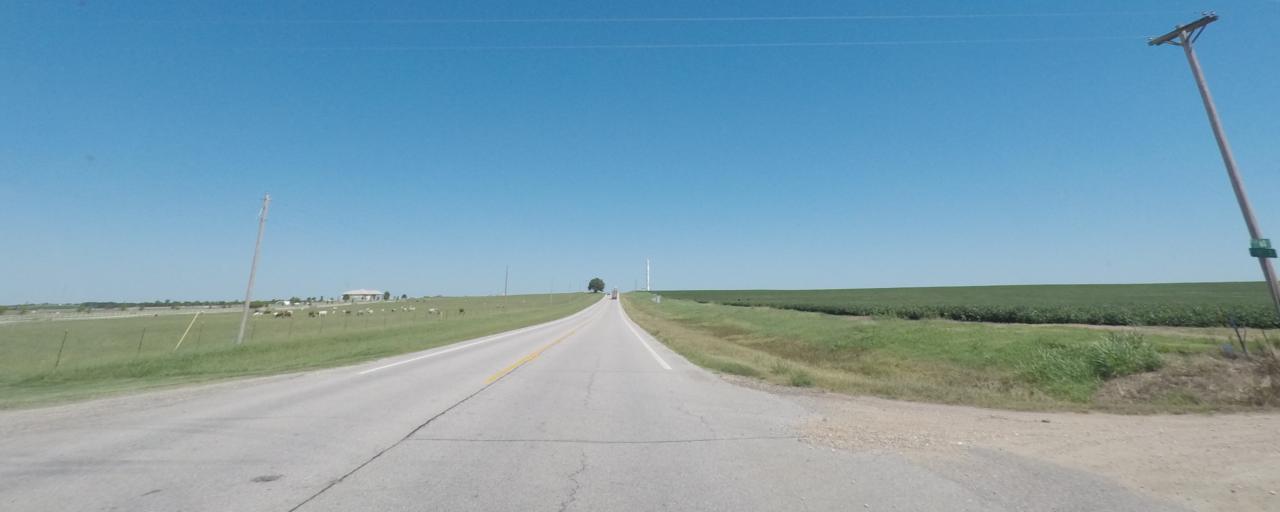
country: US
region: Kansas
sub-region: Sumner County
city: Wellington
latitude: 37.3475
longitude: -97.3851
